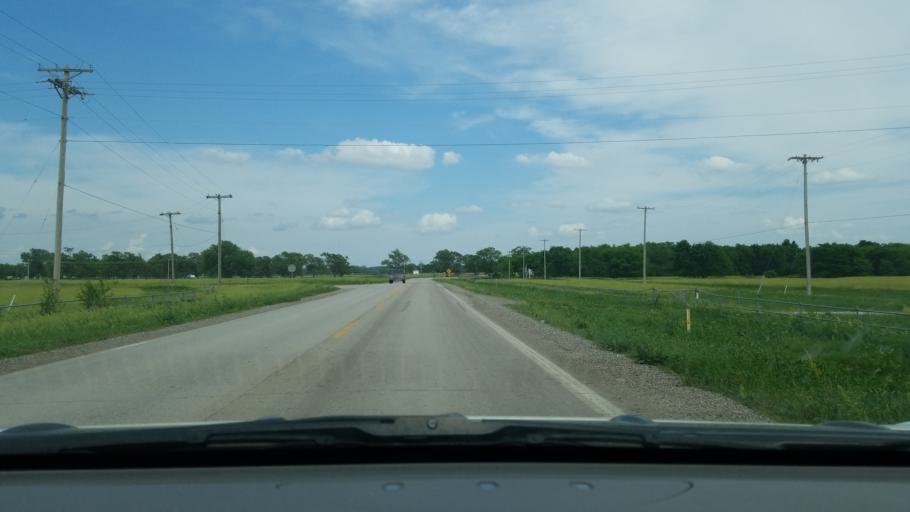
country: US
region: Nebraska
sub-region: Saunders County
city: Ashland
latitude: 41.0597
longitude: -96.3386
